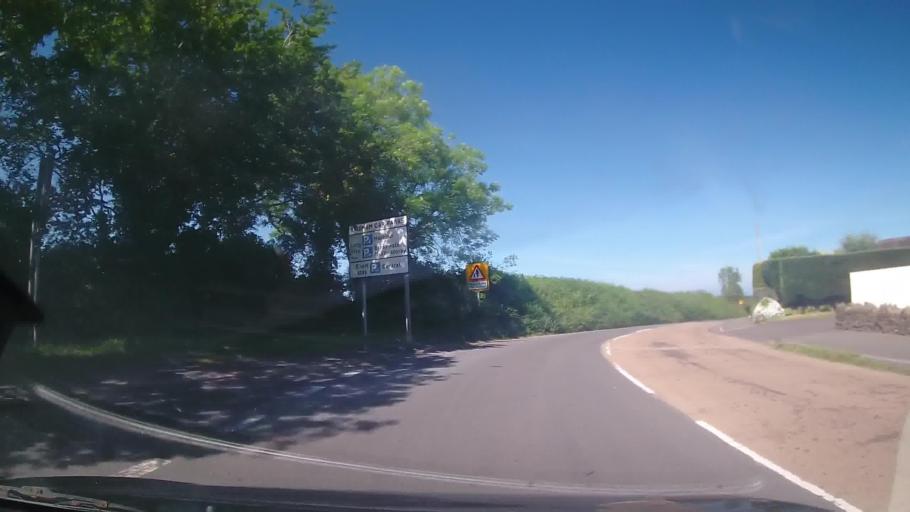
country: GB
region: England
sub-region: Borough of Torbay
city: Brixham
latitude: 50.3739
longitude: -3.5438
